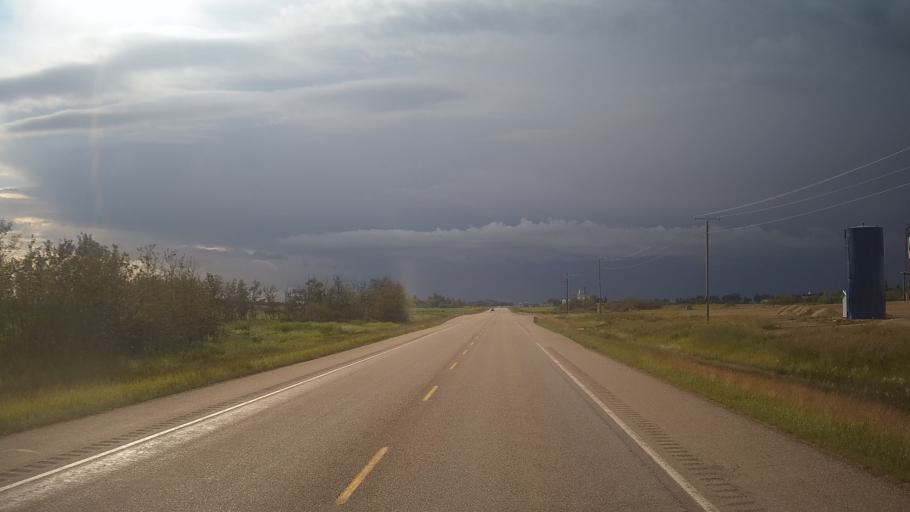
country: CA
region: Alberta
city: Vegreville
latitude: 53.2241
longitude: -112.2255
